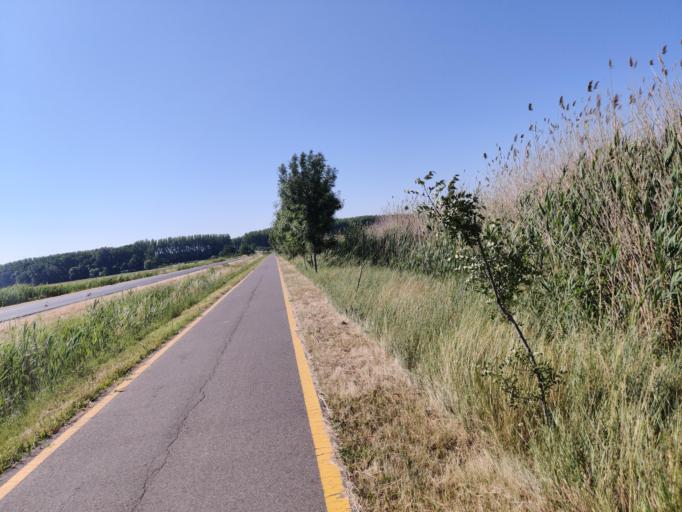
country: HU
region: Hajdu-Bihar
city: Balmazujvaros
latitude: 47.5882
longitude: 21.3444
